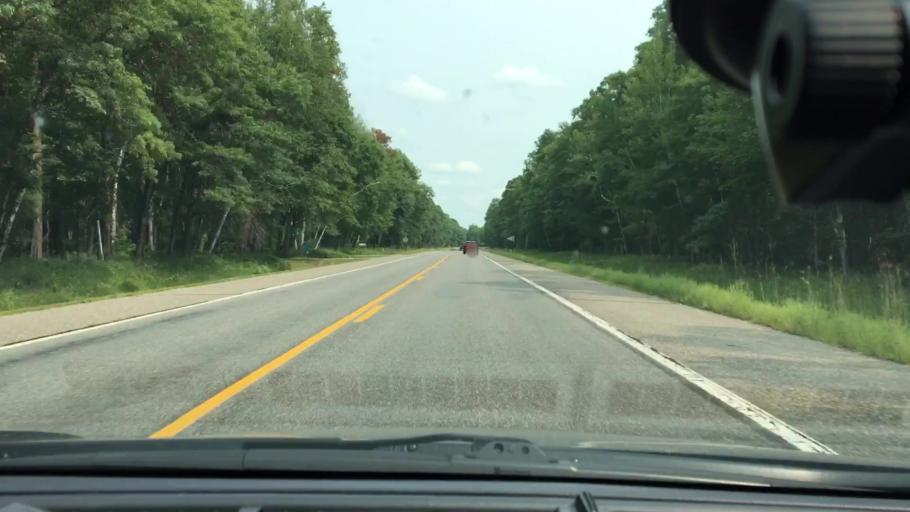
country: US
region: Minnesota
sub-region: Crow Wing County
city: Breezy Point
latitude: 46.5298
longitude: -94.1934
